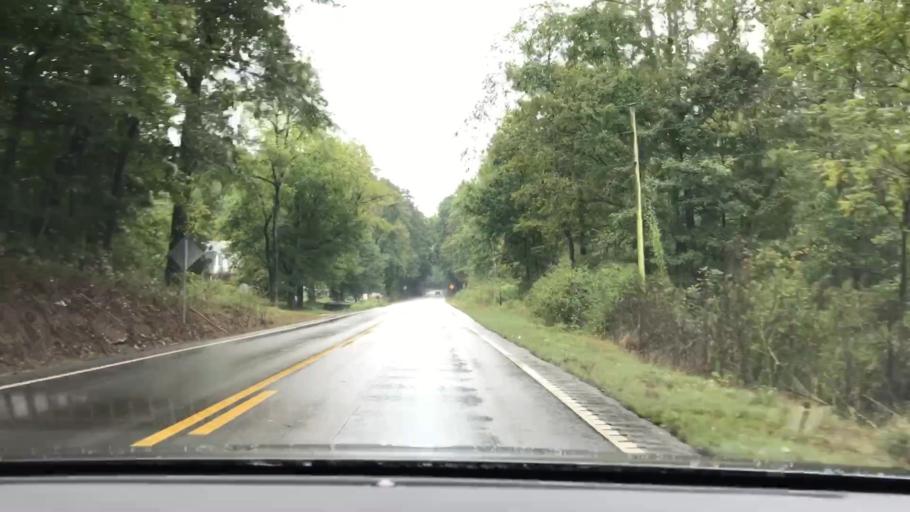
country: US
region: Tennessee
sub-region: Macon County
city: Red Boiling Springs
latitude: 36.5687
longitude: -85.7915
